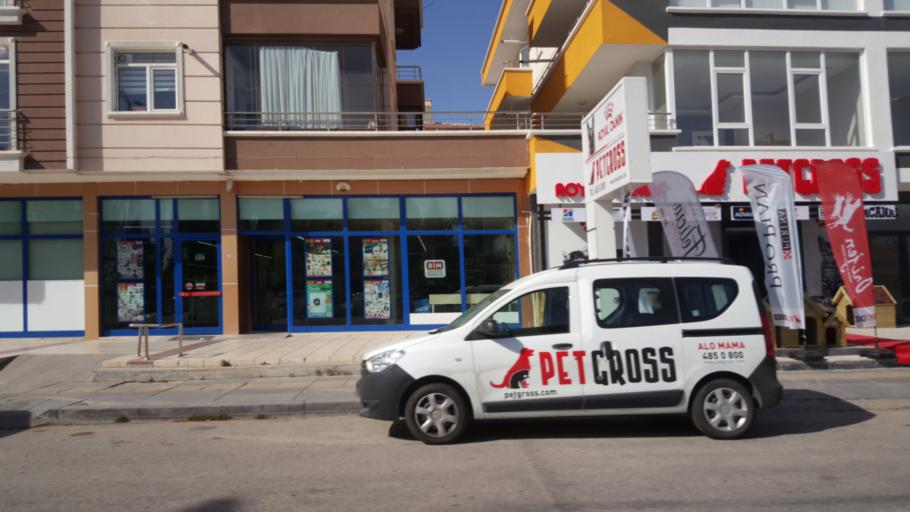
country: TR
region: Ankara
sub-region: Goelbasi
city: Golbasi
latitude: 39.7973
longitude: 32.7984
